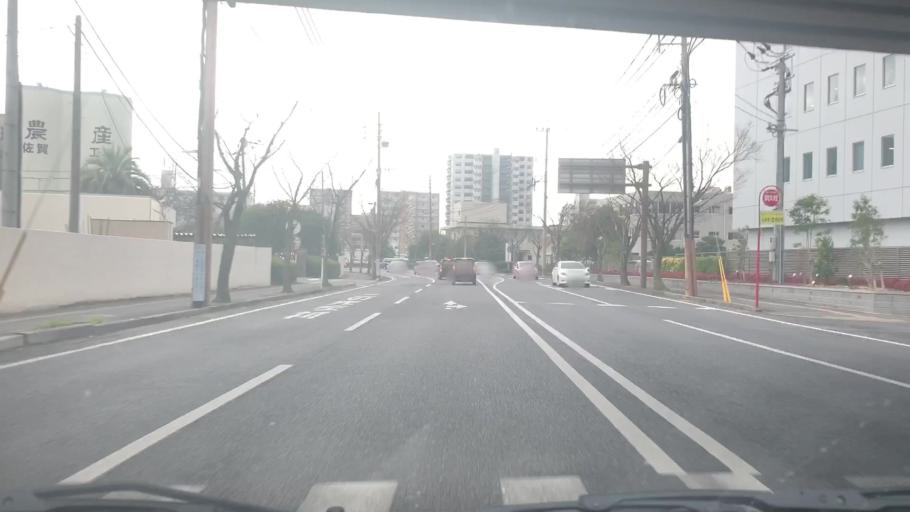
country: JP
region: Saga Prefecture
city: Saga-shi
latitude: 33.2650
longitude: 130.3020
